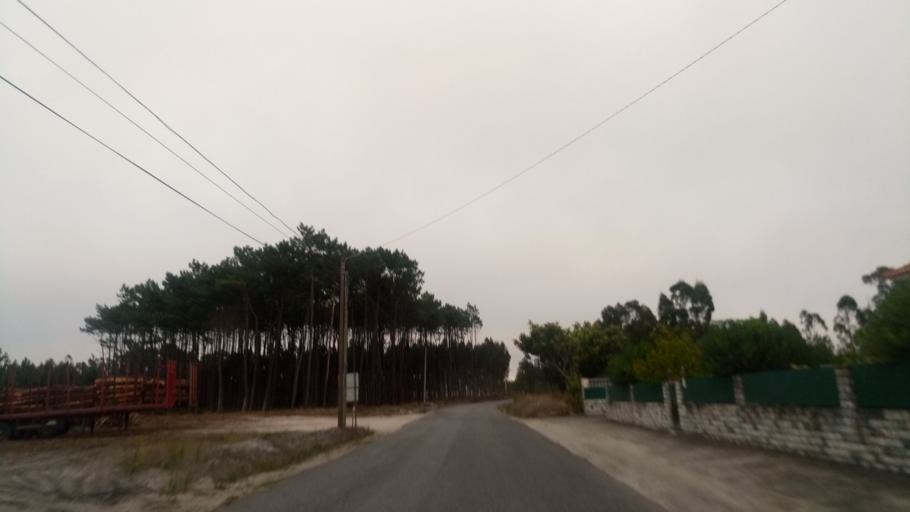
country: PT
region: Leiria
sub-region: Caldas da Rainha
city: Caldas da Rainha
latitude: 39.4462
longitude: -9.1683
